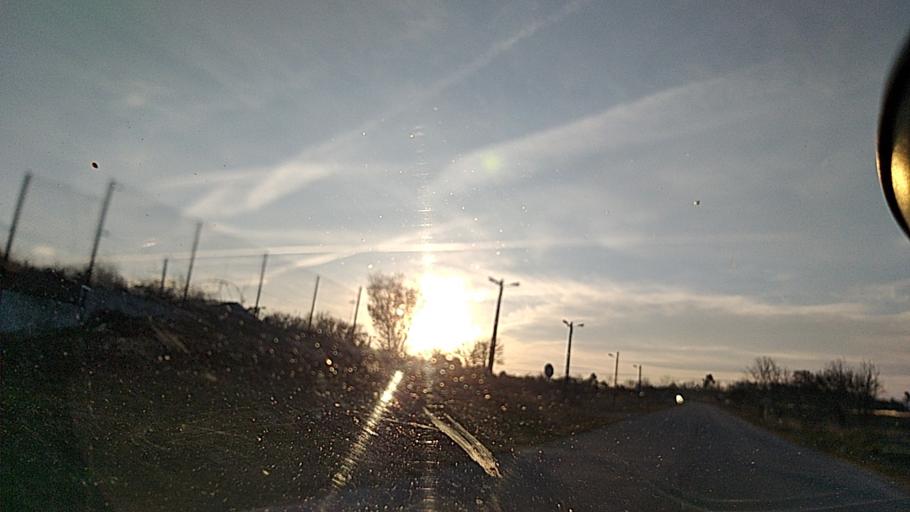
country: PT
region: Guarda
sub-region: Pinhel
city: Pinhel
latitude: 40.6043
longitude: -7.0349
